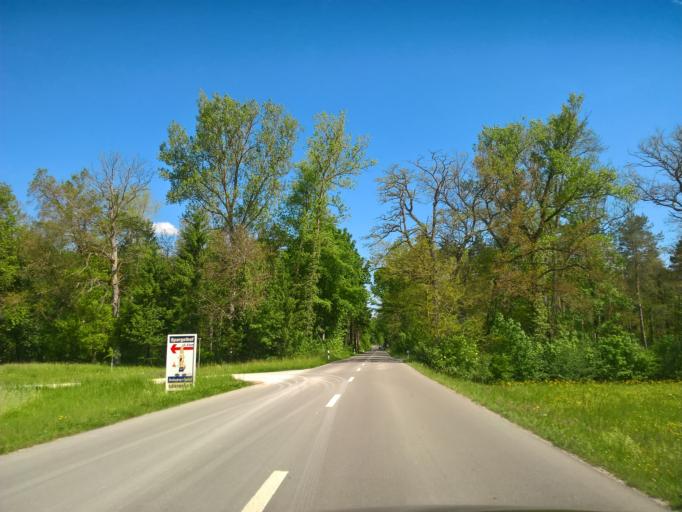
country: DE
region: Baden-Wuerttemberg
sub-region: Freiburg Region
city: Lottstetten
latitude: 47.5907
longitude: 8.6061
